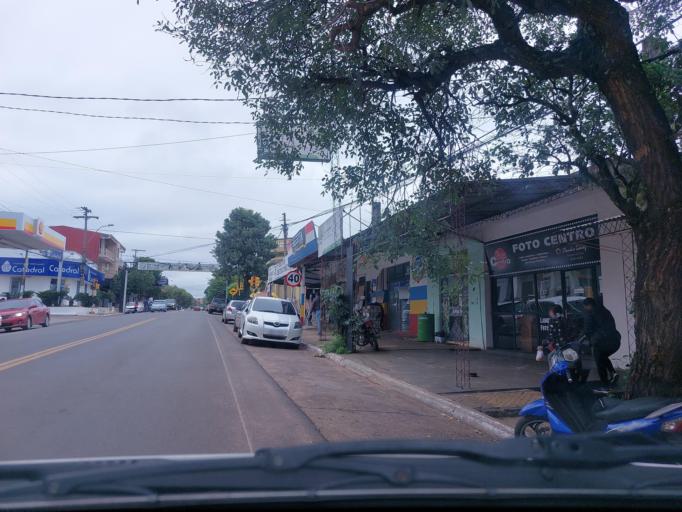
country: PY
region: San Pedro
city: Guayaybi
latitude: -24.6639
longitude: -56.4438
